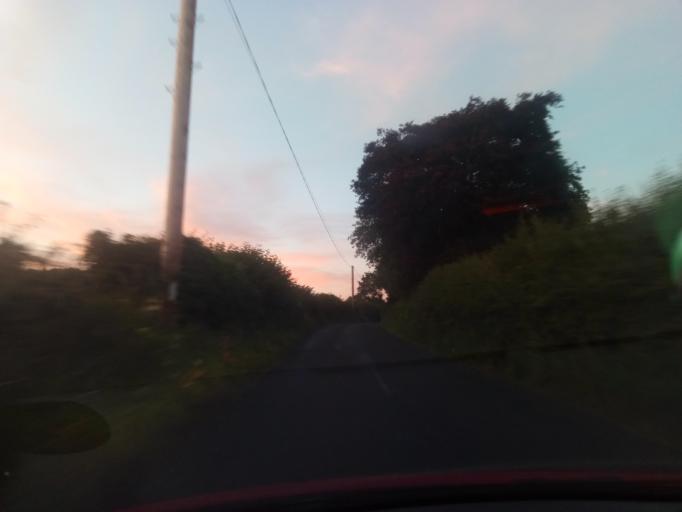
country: GB
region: England
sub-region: Northumberland
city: Warden
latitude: 54.9838
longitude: -2.2256
